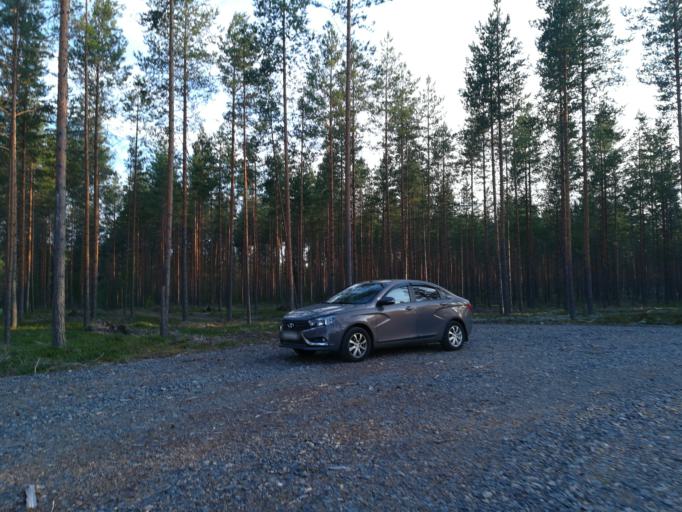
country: FI
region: Southern Savonia
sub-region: Mikkeli
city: Puumala
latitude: 61.4329
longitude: 28.4646
